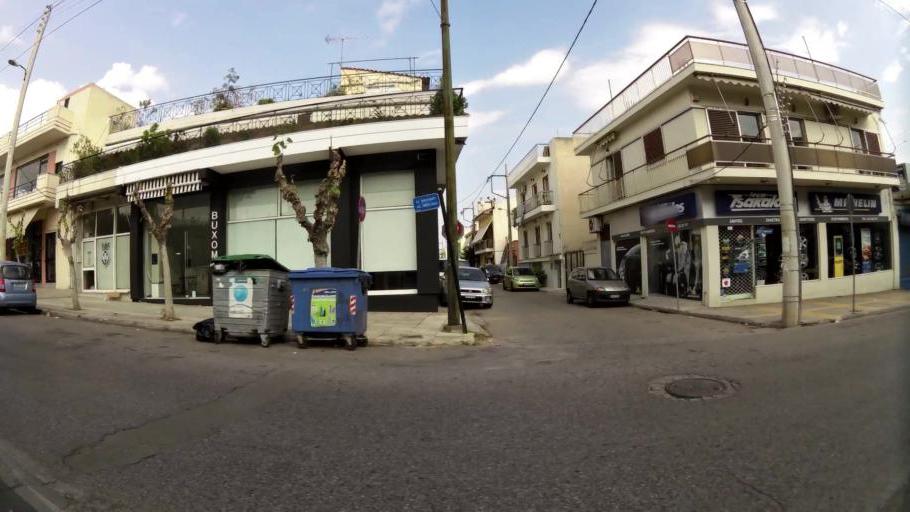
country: GR
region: Attica
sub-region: Nomarchia Athinas
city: Ilion
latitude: 38.0415
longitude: 23.7028
